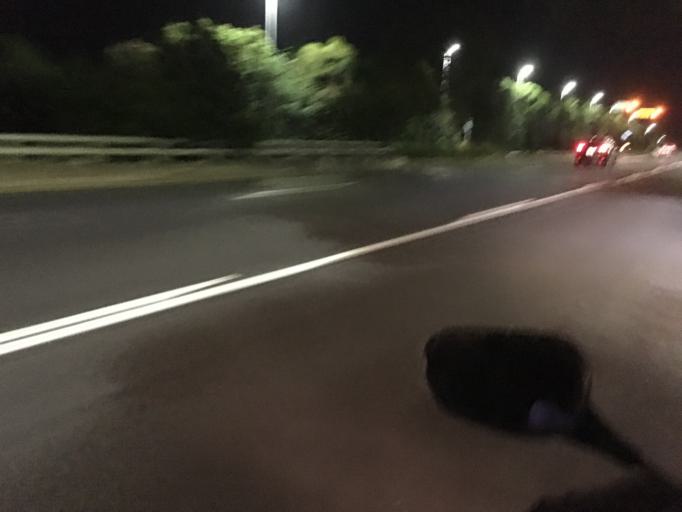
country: TW
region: Taiwan
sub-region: Hsinchu
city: Hsinchu
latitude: 24.7658
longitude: 120.9559
